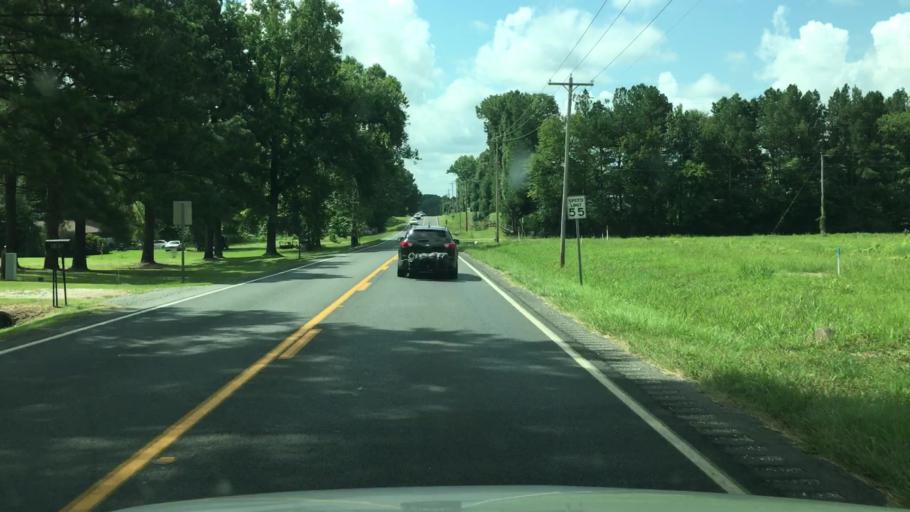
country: US
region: Arkansas
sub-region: Garland County
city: Lake Hamilton
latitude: 34.3090
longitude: -93.1679
